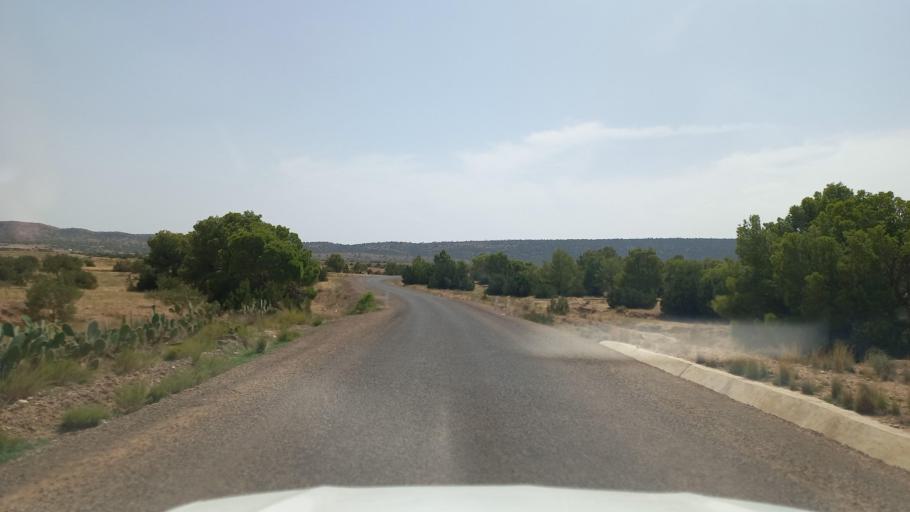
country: TN
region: Al Qasrayn
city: Sbiba
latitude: 35.3943
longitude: 8.9487
